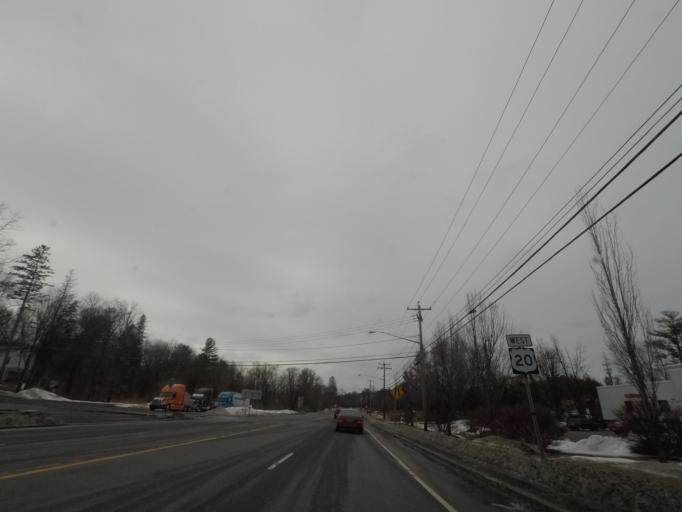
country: US
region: New York
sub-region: Albany County
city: Voorheesville
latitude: 42.7148
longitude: -73.9327
